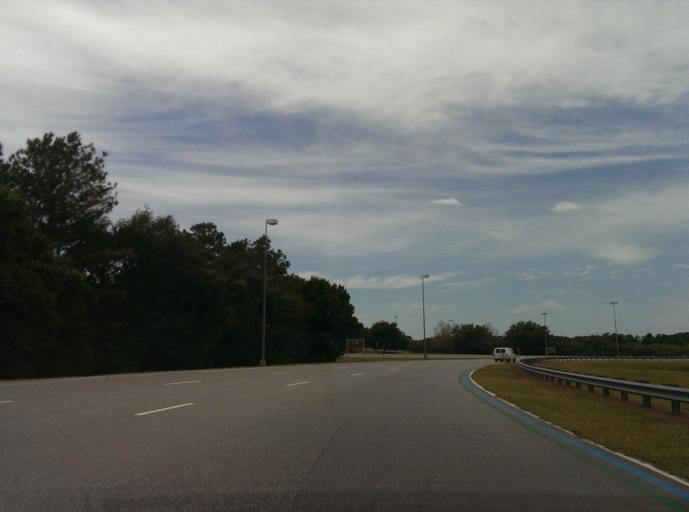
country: US
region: Florida
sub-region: Polk County
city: Citrus Ridge
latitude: 28.3491
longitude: -81.5914
